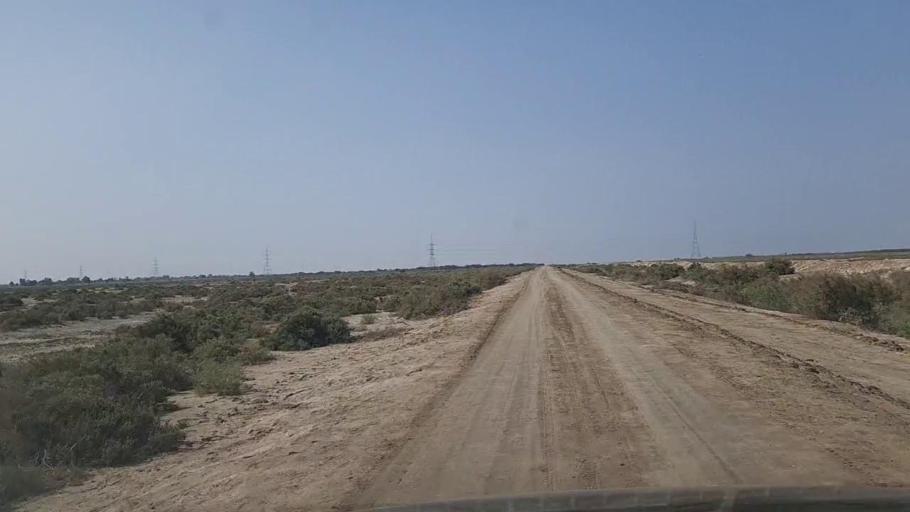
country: PK
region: Sindh
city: Gharo
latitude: 24.7075
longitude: 67.5536
